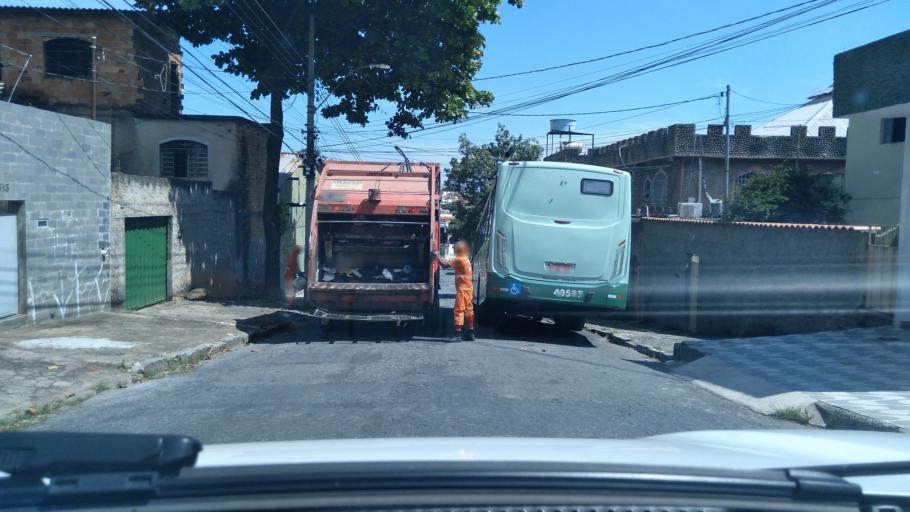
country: BR
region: Minas Gerais
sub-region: Contagem
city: Contagem
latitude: -19.9201
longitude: -44.0046
